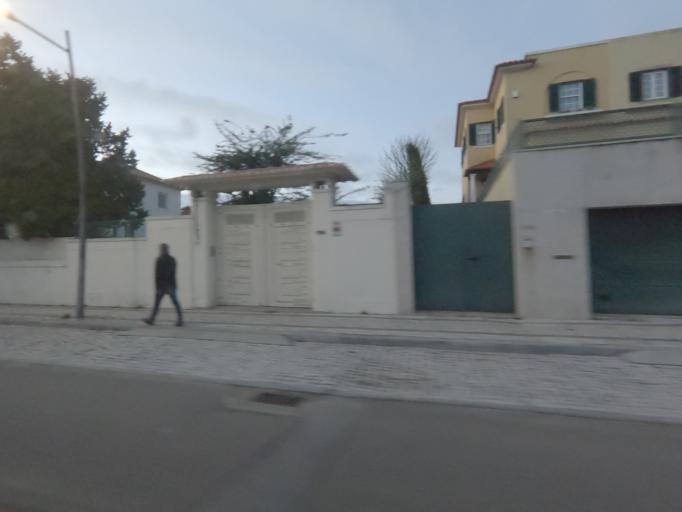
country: PT
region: Porto
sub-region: Matosinhos
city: Matosinhos
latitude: 41.1576
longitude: -8.6674
